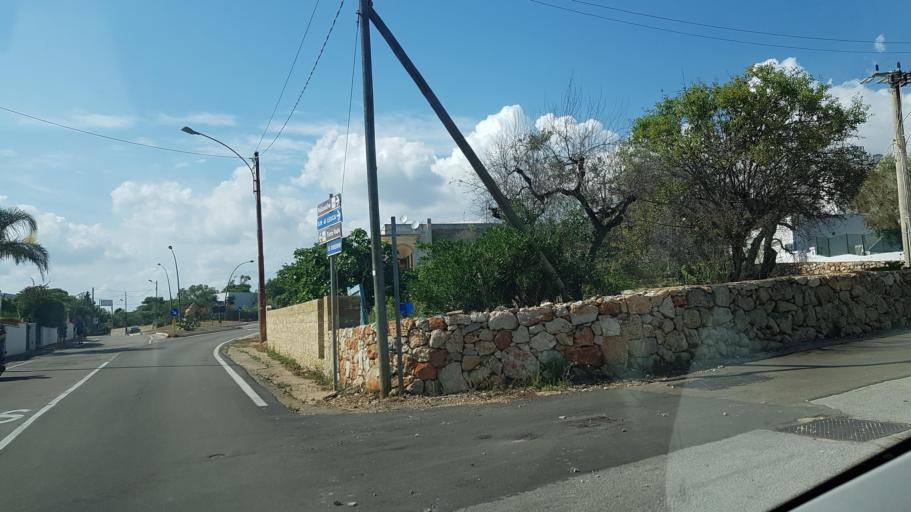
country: IT
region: Apulia
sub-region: Provincia di Lecce
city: Morciano di Leuca
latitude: 39.8142
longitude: 18.3138
